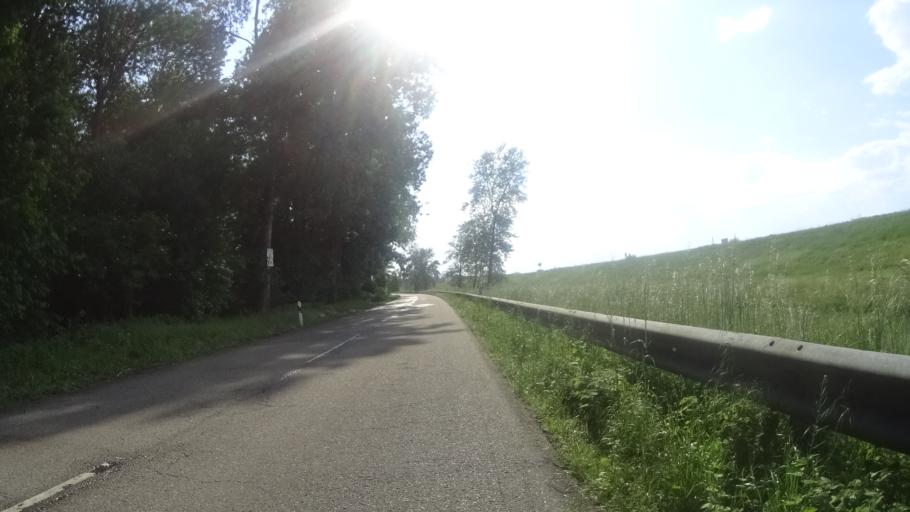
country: DE
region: Baden-Wuerttemberg
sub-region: Karlsruhe Region
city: Schwarzach
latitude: 48.7889
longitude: 8.0421
